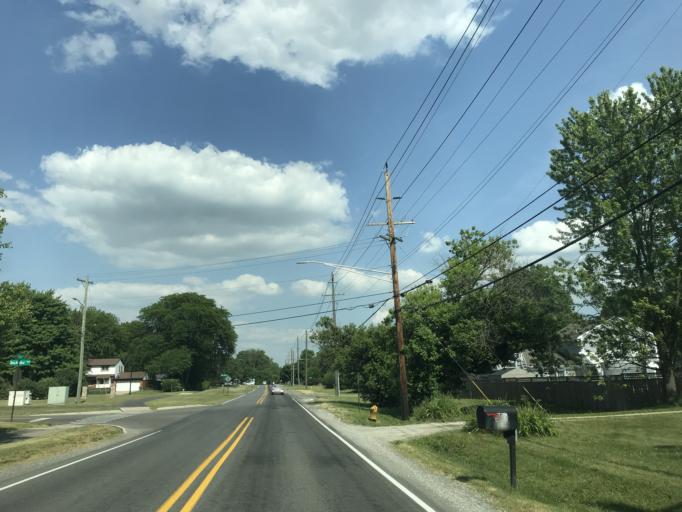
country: US
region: Michigan
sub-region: Washtenaw County
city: Ypsilanti
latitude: 42.2611
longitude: -83.5947
